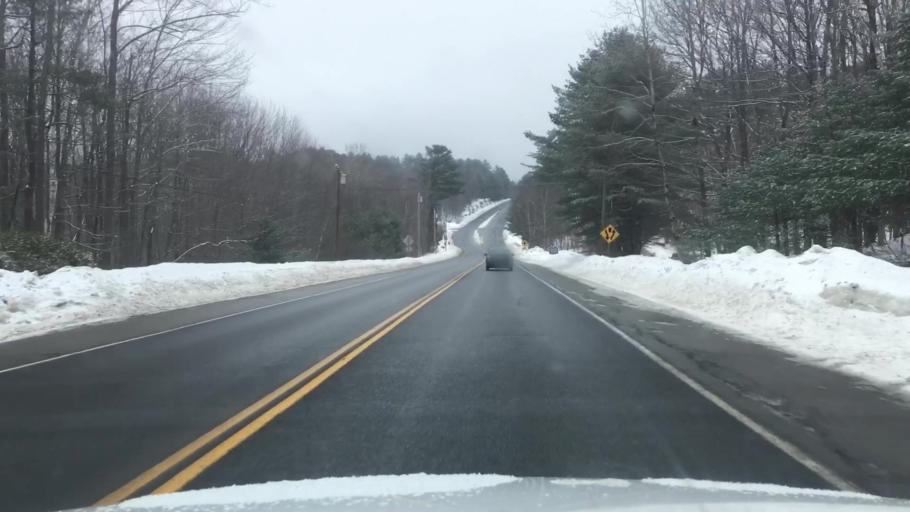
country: US
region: Maine
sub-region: Franklin County
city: Wilton
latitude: 44.5838
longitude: -70.2394
